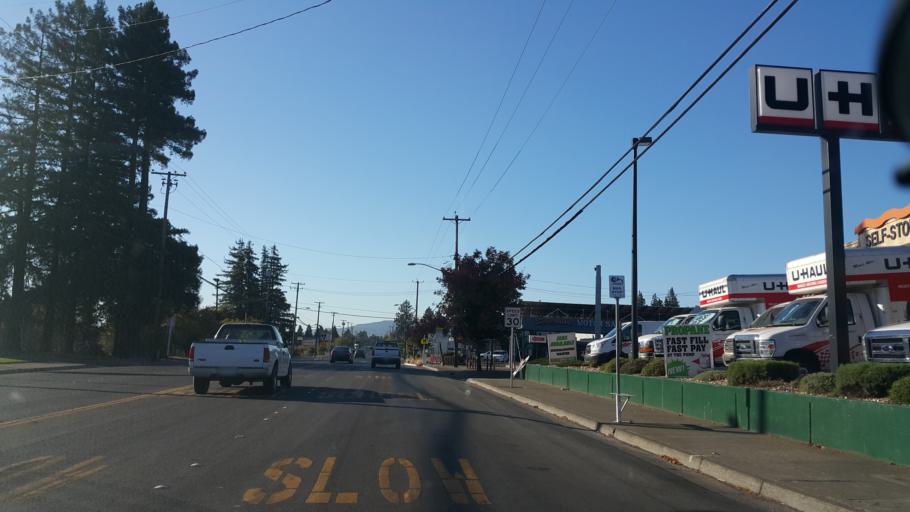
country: US
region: California
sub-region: Mendocino County
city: Ukiah
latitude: 39.1655
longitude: -123.2108
